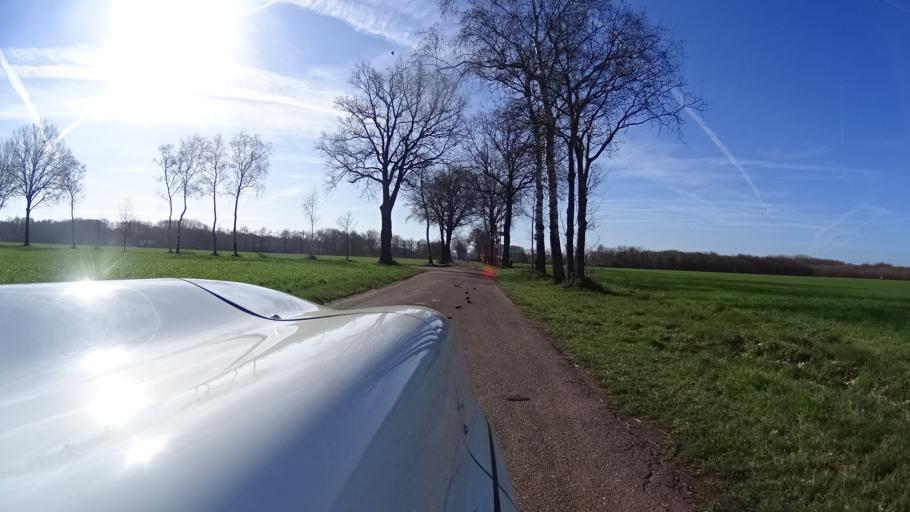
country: NL
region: North Brabant
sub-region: Gemeente Uden
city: Odiliapeel
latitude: 51.6650
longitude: 5.6870
